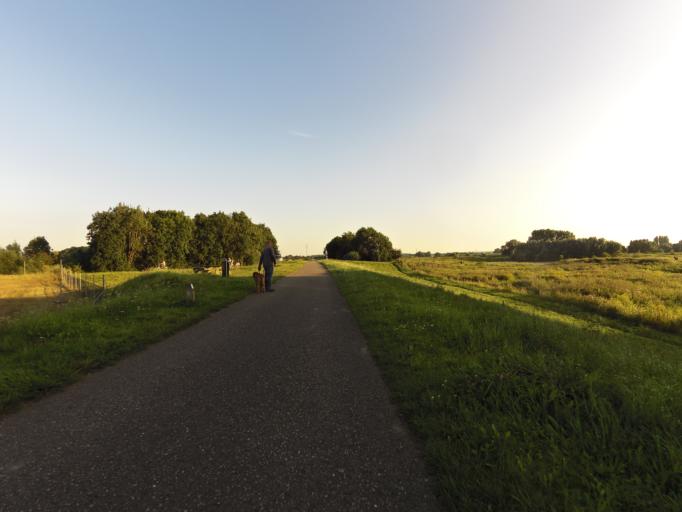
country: NL
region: Gelderland
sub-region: Gemeente Duiven
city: Duiven
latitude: 51.9166
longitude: 5.9967
